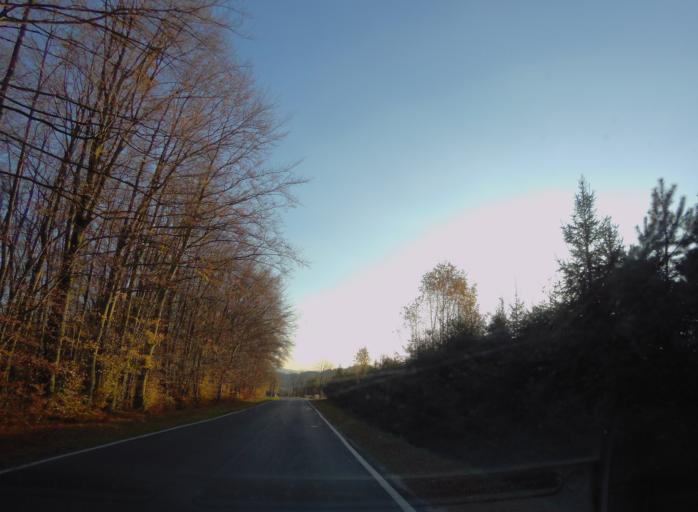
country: PL
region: Subcarpathian Voivodeship
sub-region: Powiat leski
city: Polanczyk
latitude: 49.3856
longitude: 22.4300
